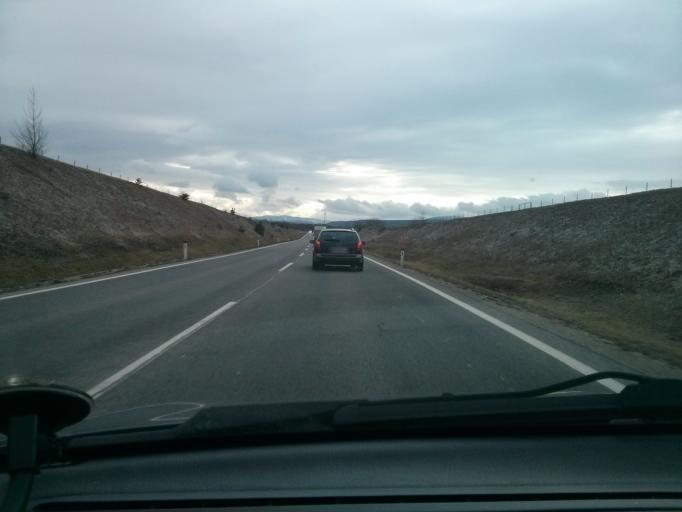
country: AT
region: Lower Austria
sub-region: Politischer Bezirk Wiener Neustadt
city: Theresienfeld
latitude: 47.8523
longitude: 16.2110
